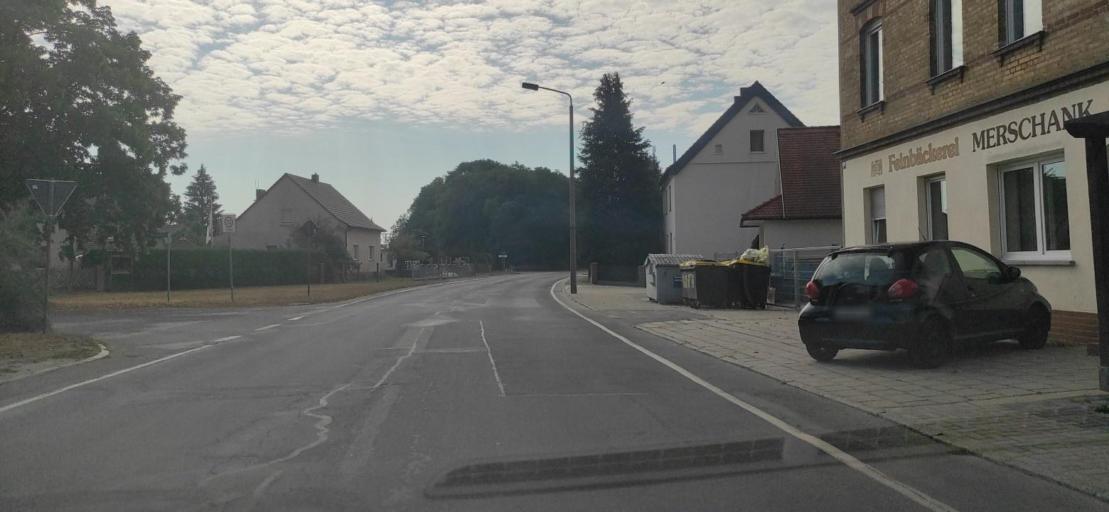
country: DE
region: Brandenburg
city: Forst
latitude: 51.7174
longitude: 14.6629
